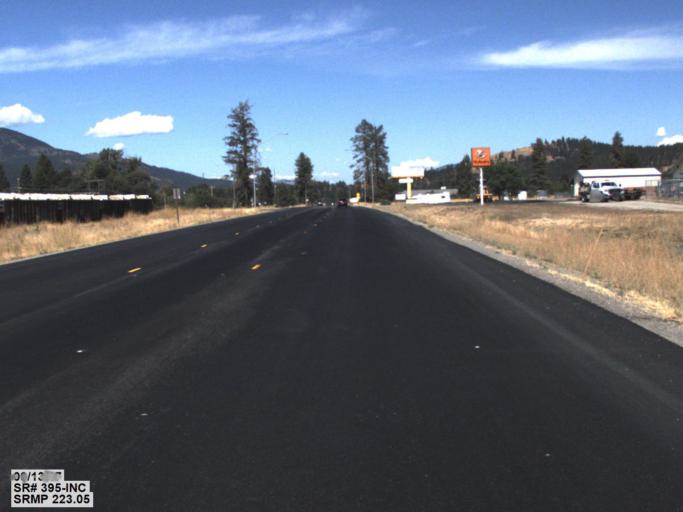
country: US
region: Washington
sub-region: Stevens County
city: Colville
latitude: 48.4559
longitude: -117.8785
